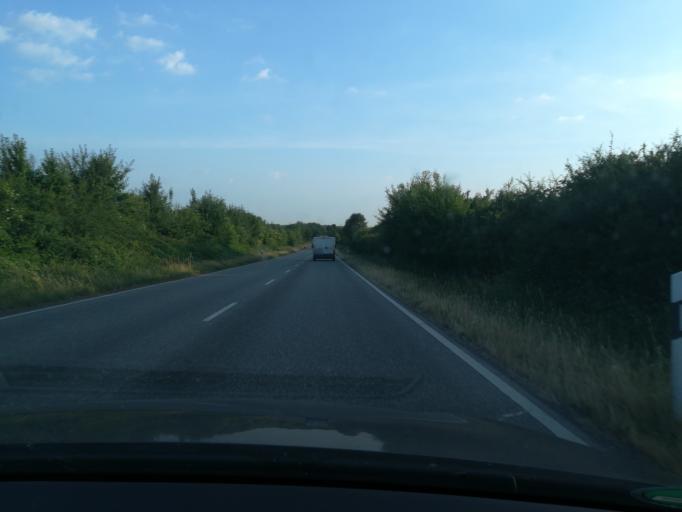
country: DE
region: Schleswig-Holstein
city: Siek
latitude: 53.6382
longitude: 10.3064
